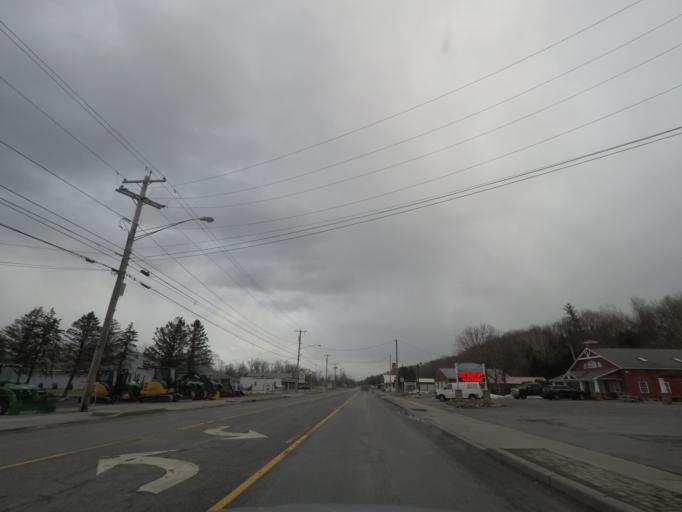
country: US
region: New York
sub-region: Madison County
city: Chittenango
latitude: 43.0541
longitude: -75.8623
